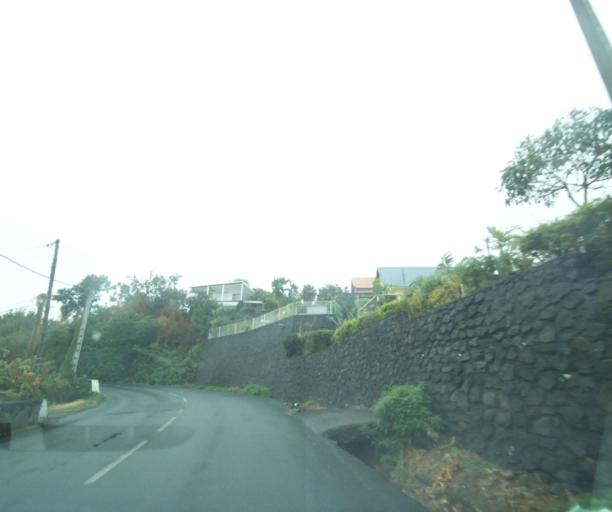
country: RE
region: Reunion
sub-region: Reunion
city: Saint-Paul
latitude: -21.0225
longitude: 55.2916
